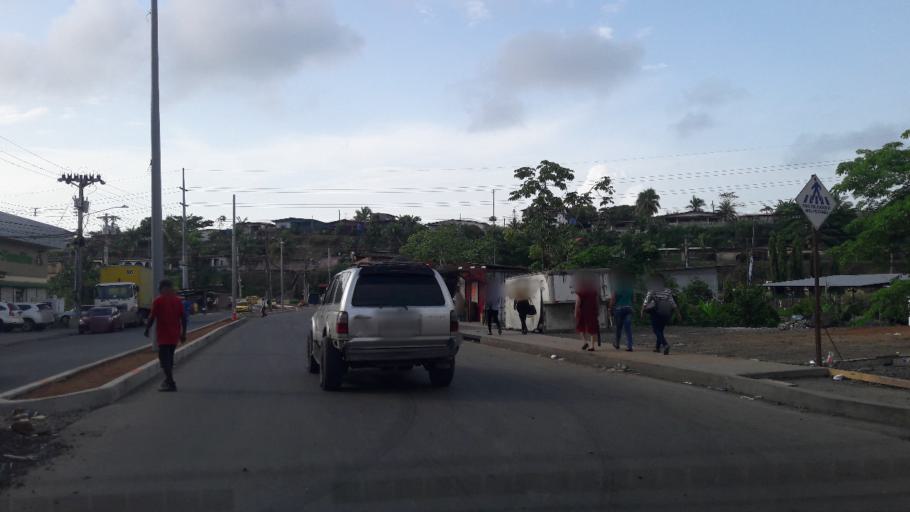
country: PA
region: Colon
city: Cativa
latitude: 9.3551
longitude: -79.8511
